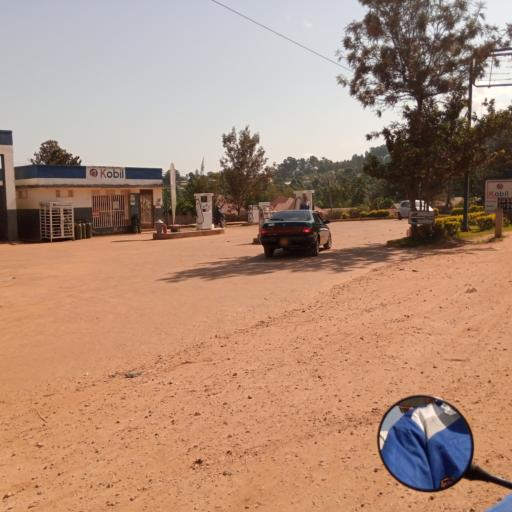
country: UG
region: Central Region
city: Masaka
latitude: -0.3442
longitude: 31.7289
